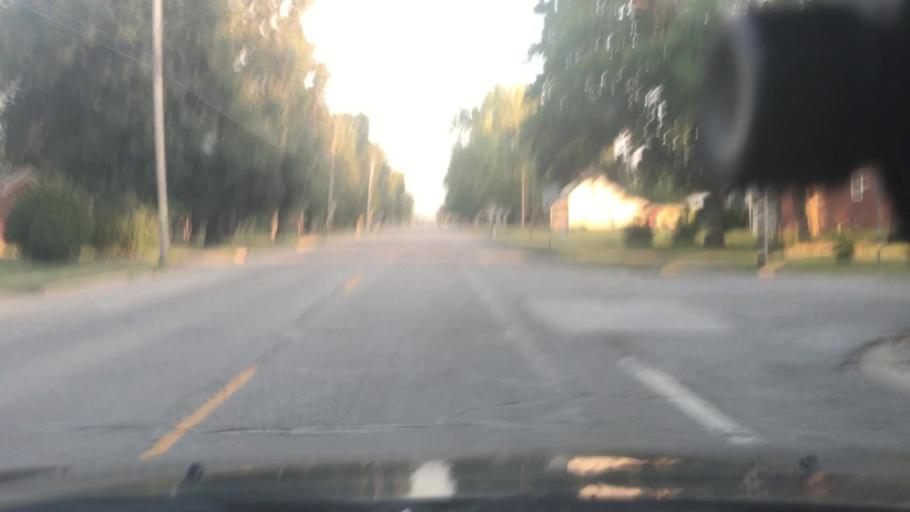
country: US
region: Illinois
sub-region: Washington County
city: Okawville
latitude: 38.4277
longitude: -89.5506
